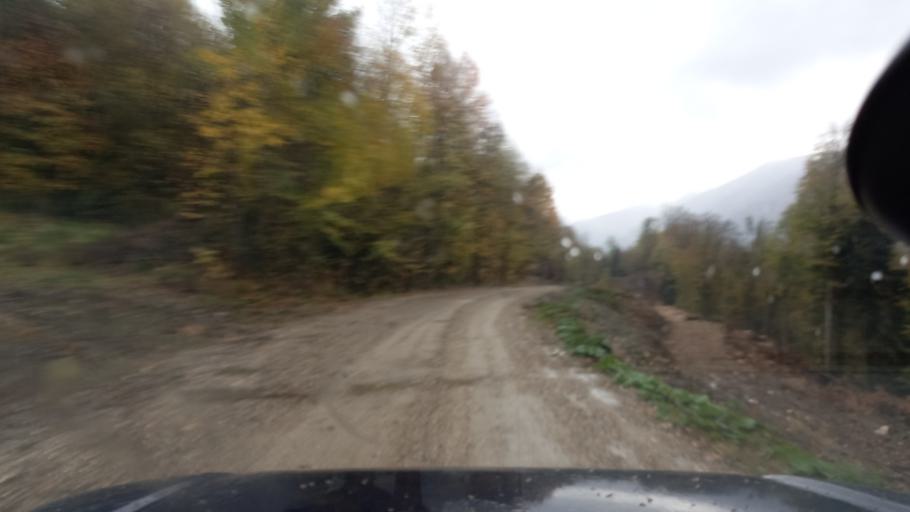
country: RU
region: Krasnodarskiy
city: Neftegorsk
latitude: 44.0441
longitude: 39.8342
